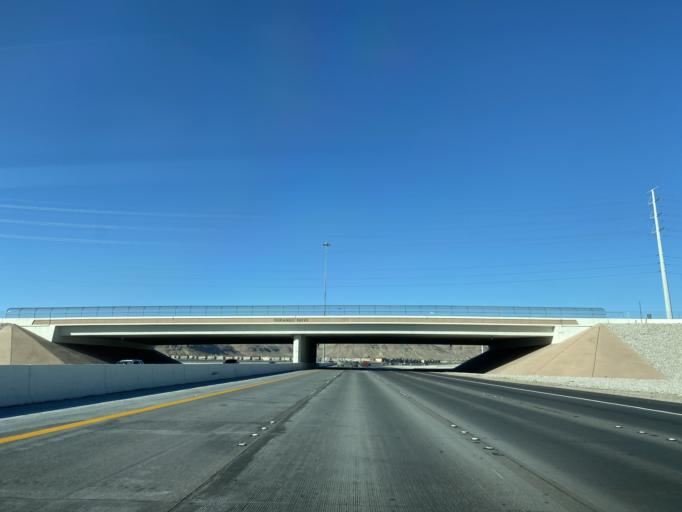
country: US
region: Nevada
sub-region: Clark County
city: Spring Valley
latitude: 36.0668
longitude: -115.2782
